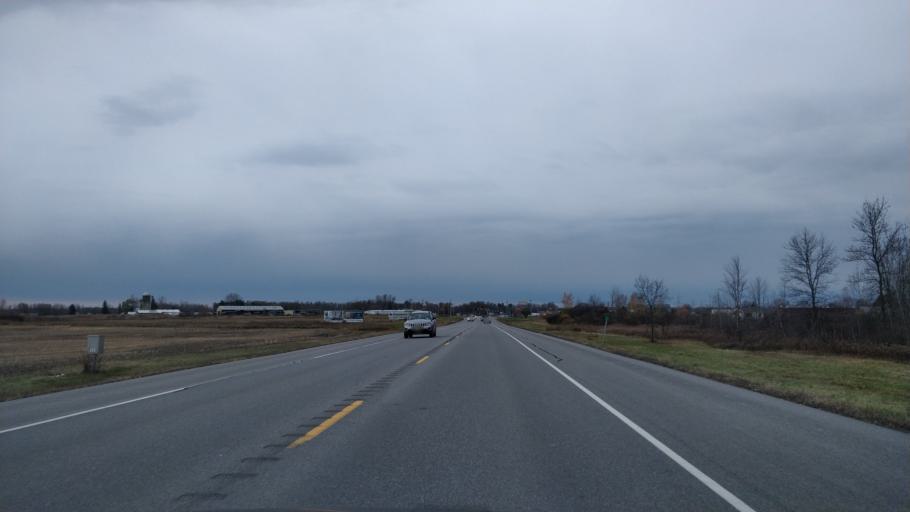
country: US
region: New York
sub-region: St. Lawrence County
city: Ogdensburg
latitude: 44.6960
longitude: -75.4674
